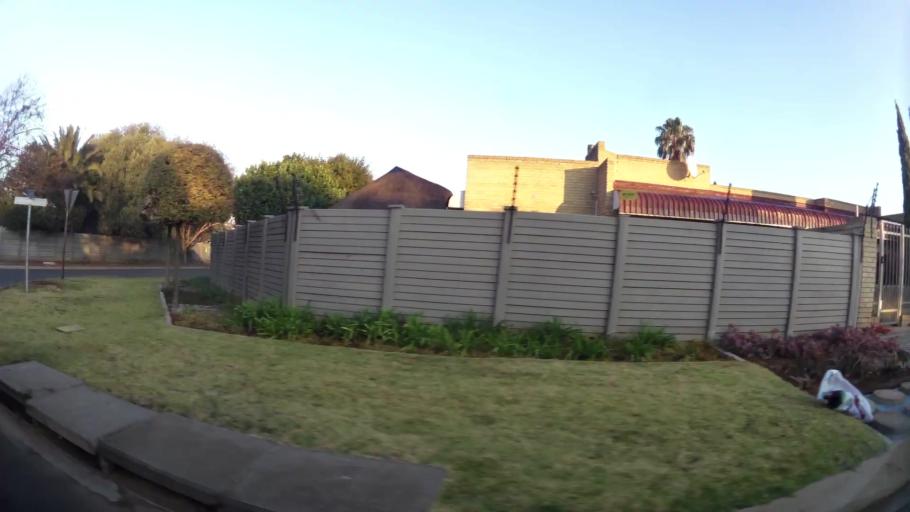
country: ZA
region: Orange Free State
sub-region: Mangaung Metropolitan Municipality
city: Bloemfontein
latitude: -29.1039
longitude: 26.1548
